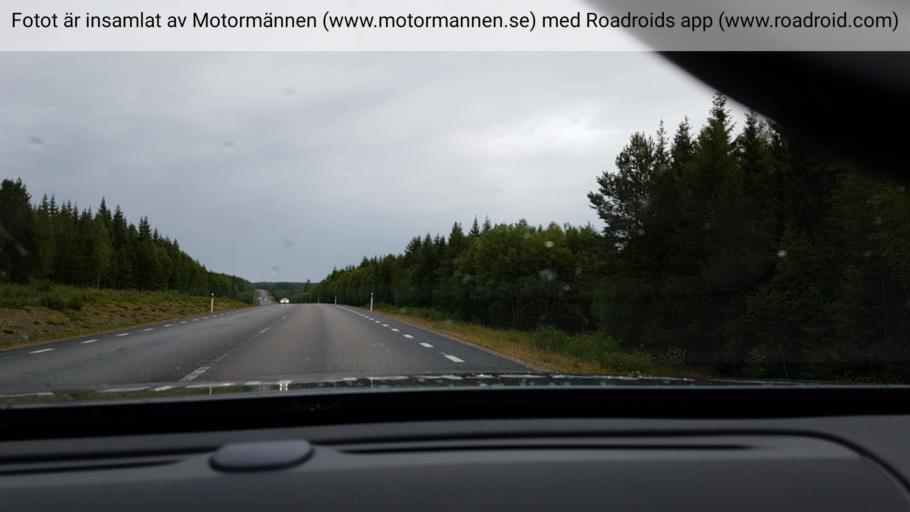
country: SE
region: Dalarna
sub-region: Rattviks Kommun
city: Raettvik
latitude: 60.8387
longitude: 15.2161
